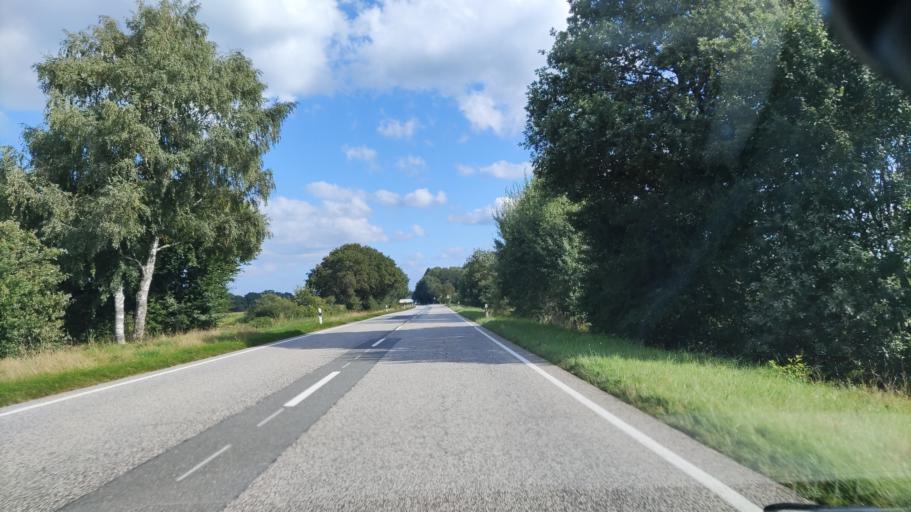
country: DE
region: Schleswig-Holstein
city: Jevenstedt
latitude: 54.2253
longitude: 9.6992
